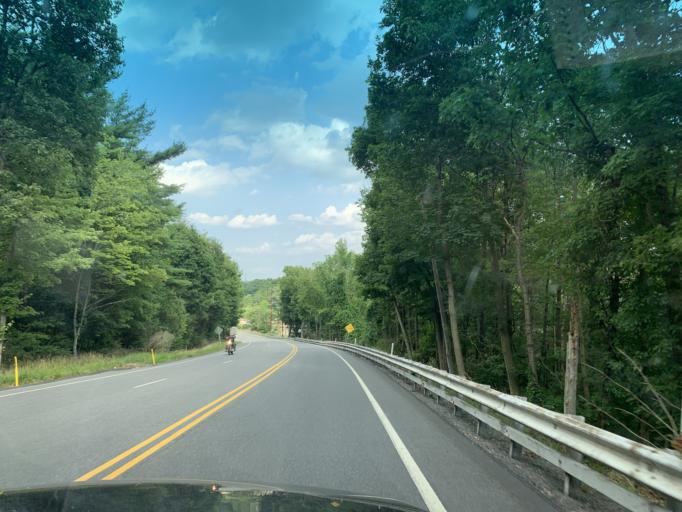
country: US
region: Pennsylvania
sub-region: Schuylkill County
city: Frackville
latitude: 40.7808
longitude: -76.2521
